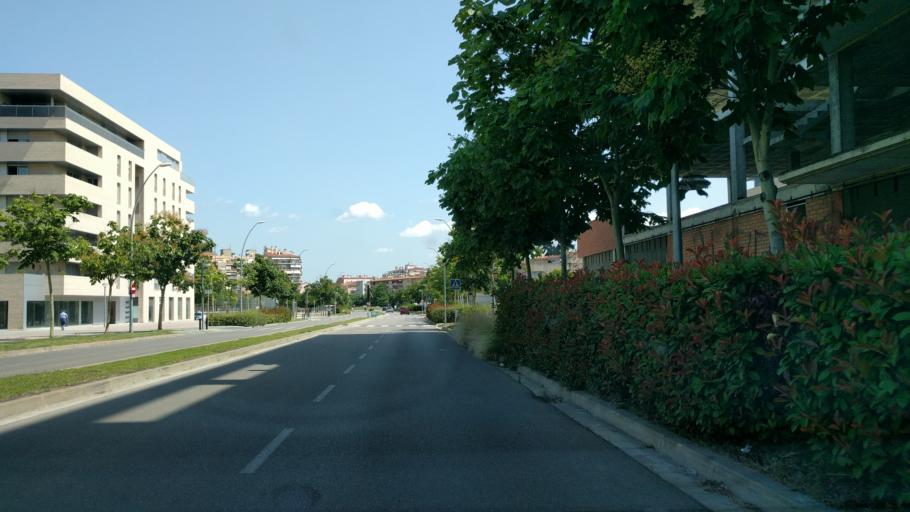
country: ES
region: Catalonia
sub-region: Provincia de Girona
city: Salt
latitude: 41.9715
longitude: 2.8004
